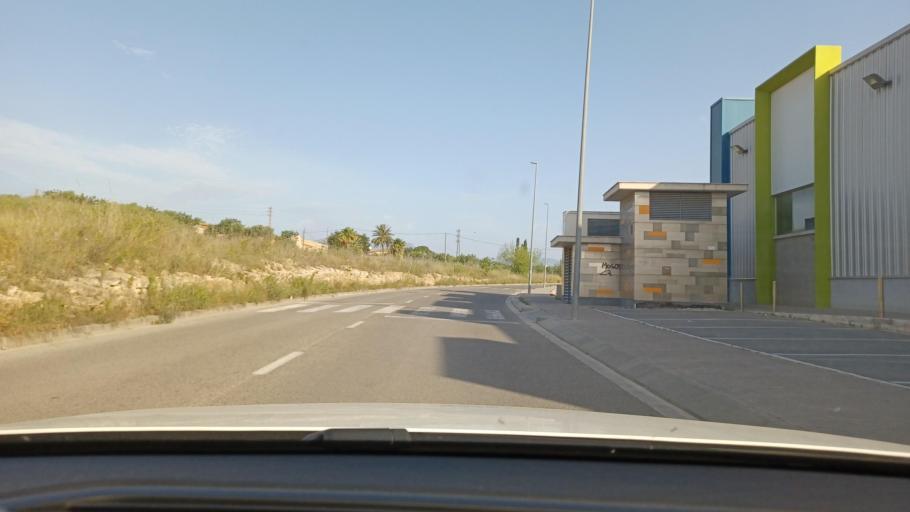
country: ES
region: Catalonia
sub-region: Provincia de Tarragona
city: Amposta
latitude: 40.7086
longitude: 0.5689
